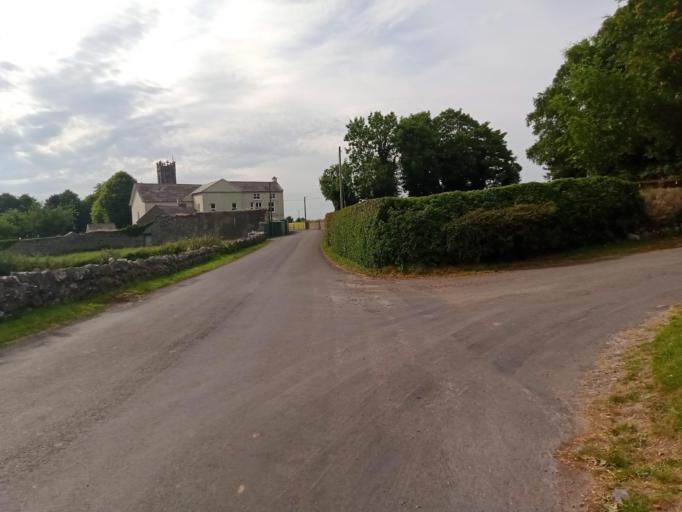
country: IE
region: Leinster
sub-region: Laois
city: Rathdowney
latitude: 52.8219
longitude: -7.4802
